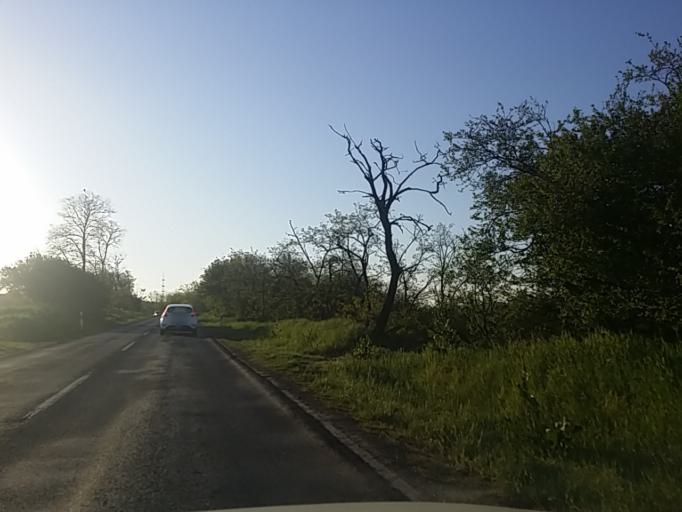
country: HU
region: Pest
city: Mogyorod
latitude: 47.6008
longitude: 19.2172
